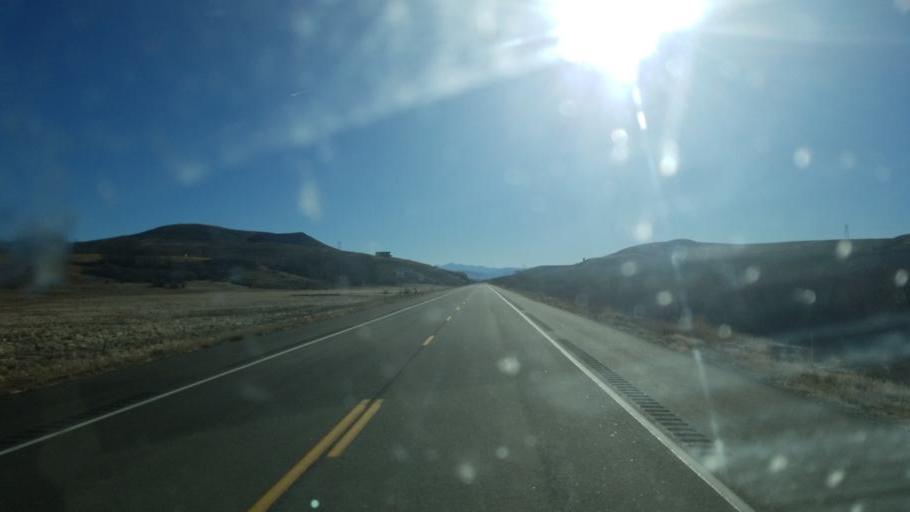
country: US
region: Colorado
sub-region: Gunnison County
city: Gunnison
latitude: 38.4976
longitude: -106.7220
